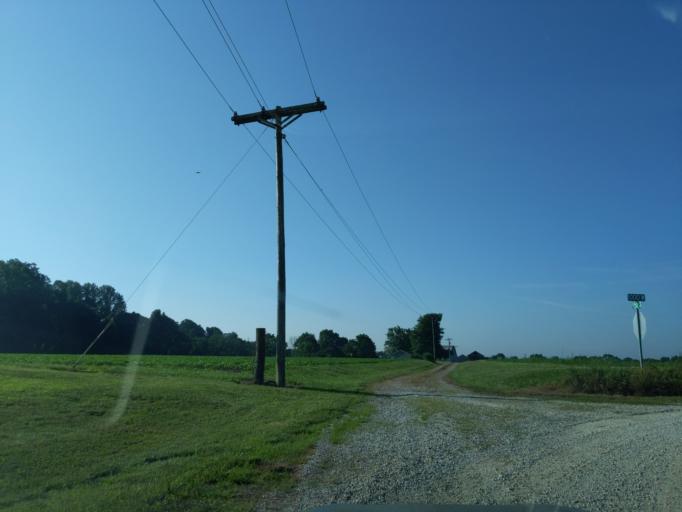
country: US
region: Indiana
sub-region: Decatur County
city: Westport
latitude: 39.1987
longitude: -85.4350
